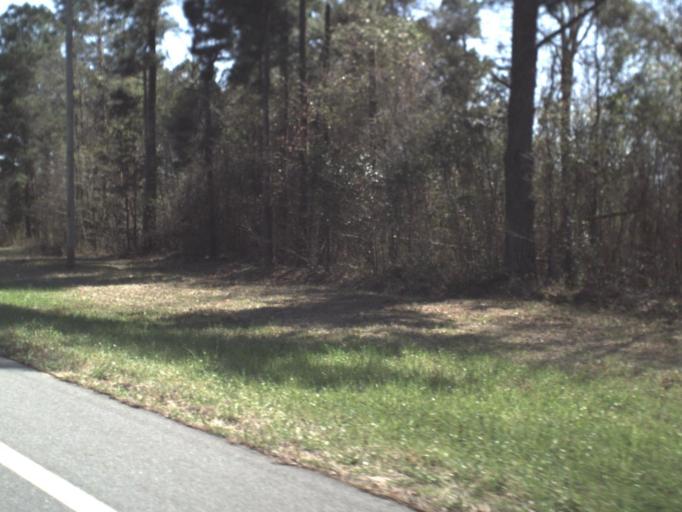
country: US
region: Florida
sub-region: Gadsden County
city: Gretna
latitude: 30.6798
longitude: -84.7098
